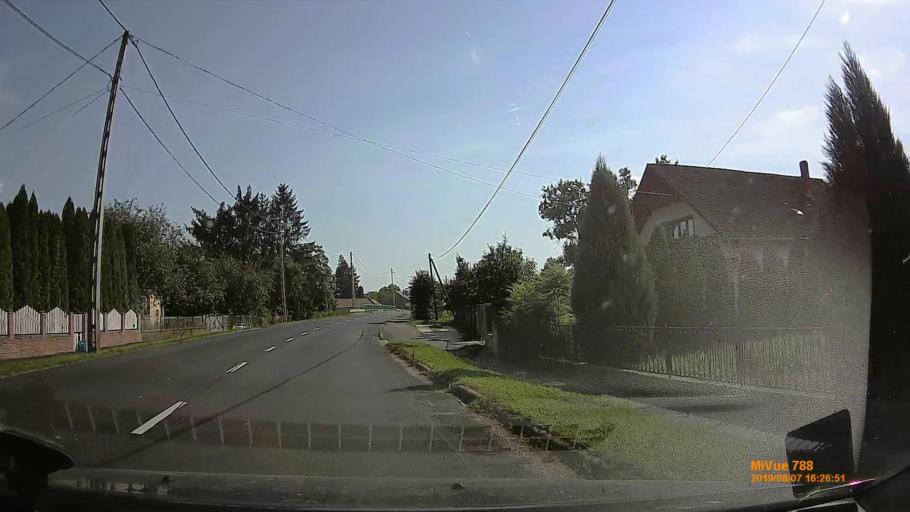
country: HU
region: Zala
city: Lenti
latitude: 46.7064
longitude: 16.5518
